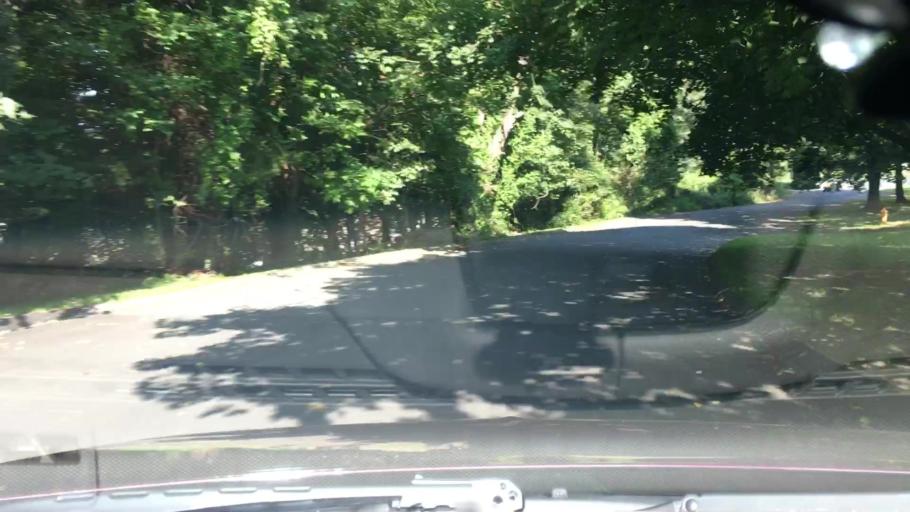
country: US
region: Connecticut
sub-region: Fairfield County
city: Bethel
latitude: 41.4081
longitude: -73.4055
